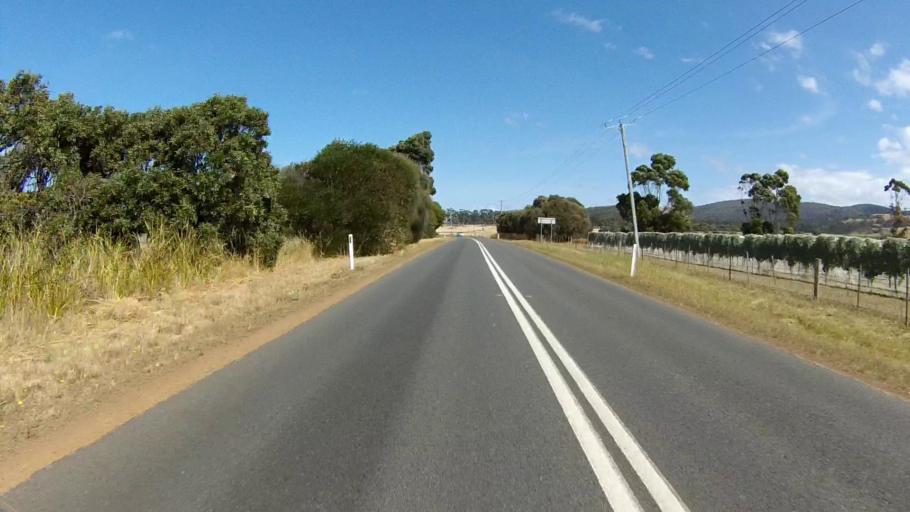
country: AU
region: Tasmania
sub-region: Sorell
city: Sorell
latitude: -42.2016
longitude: 148.0443
